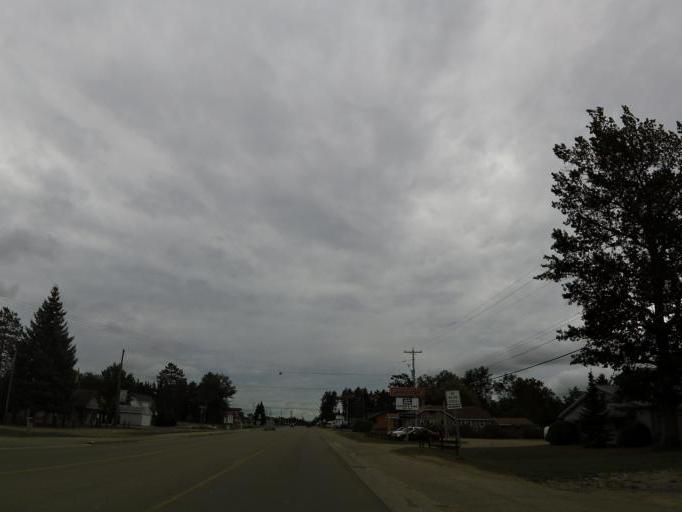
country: US
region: Michigan
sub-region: Roscommon County
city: Saint Helen
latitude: 44.3574
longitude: -84.4103
